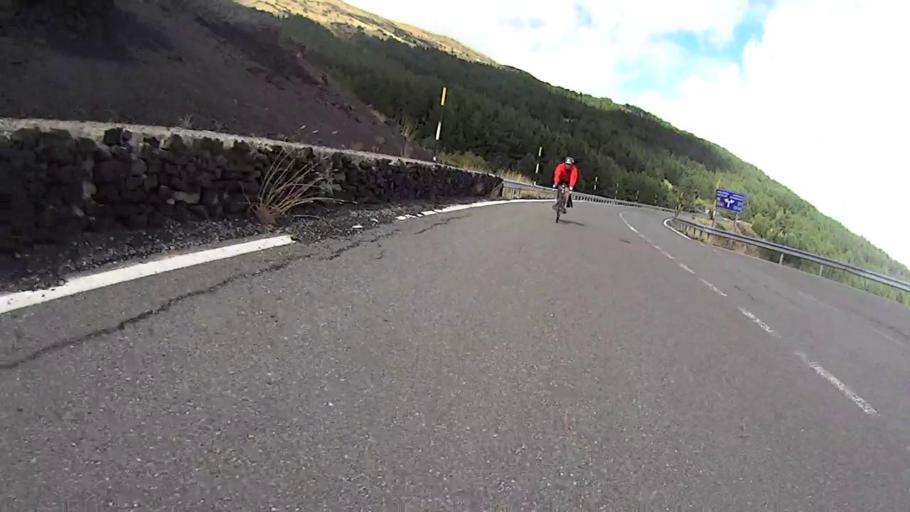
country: IT
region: Sicily
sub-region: Catania
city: Nicolosi
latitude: 37.6997
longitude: 15.0127
